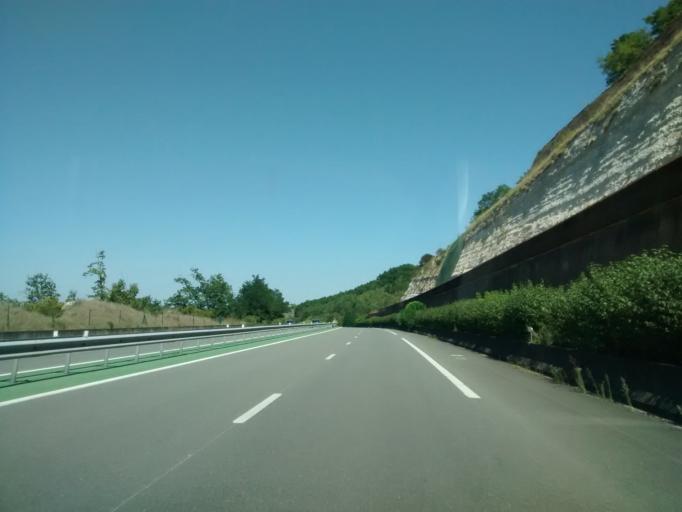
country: FR
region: Aquitaine
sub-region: Departement de la Dordogne
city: Saint-Astier
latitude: 45.1240
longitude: 0.5261
